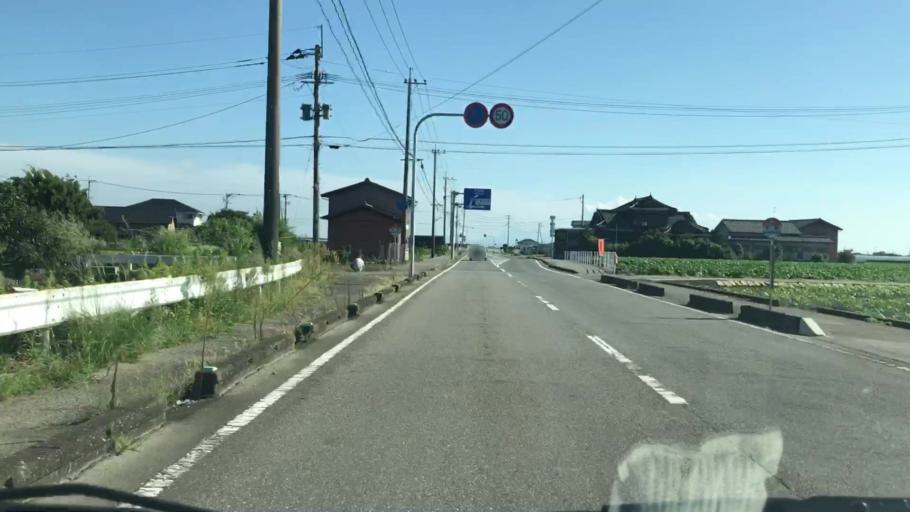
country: JP
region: Saga Prefecture
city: Okawa
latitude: 33.1990
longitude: 130.3351
